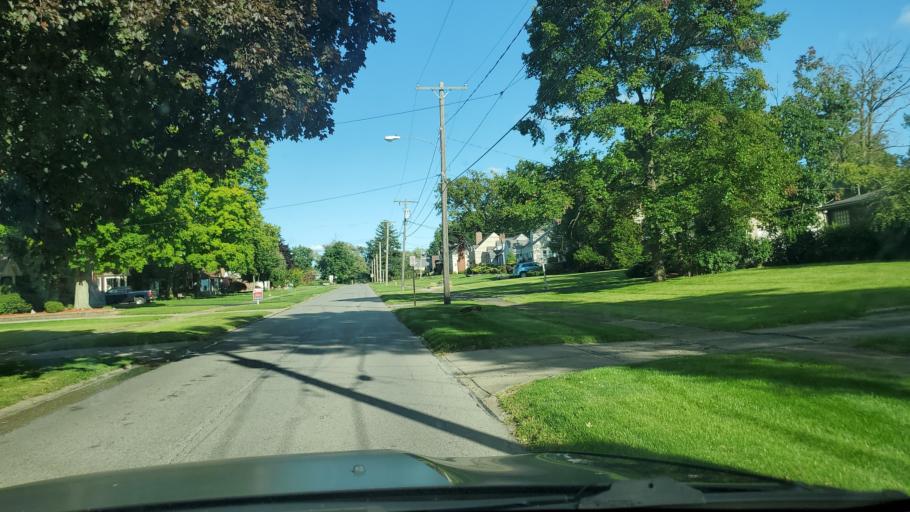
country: US
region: Ohio
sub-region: Mahoning County
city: Boardman
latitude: 41.0276
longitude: -80.6613
